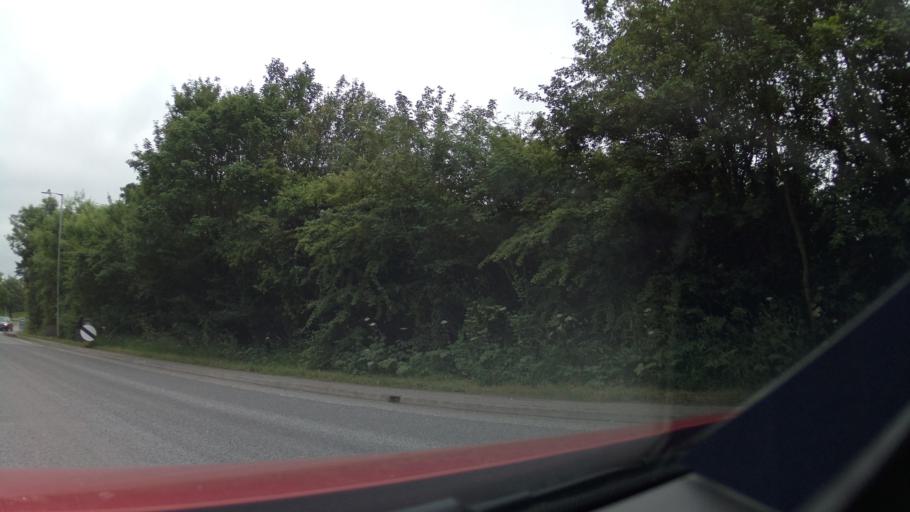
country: GB
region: England
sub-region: District of Rutland
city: Uppingham
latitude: 52.5971
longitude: -0.7268
